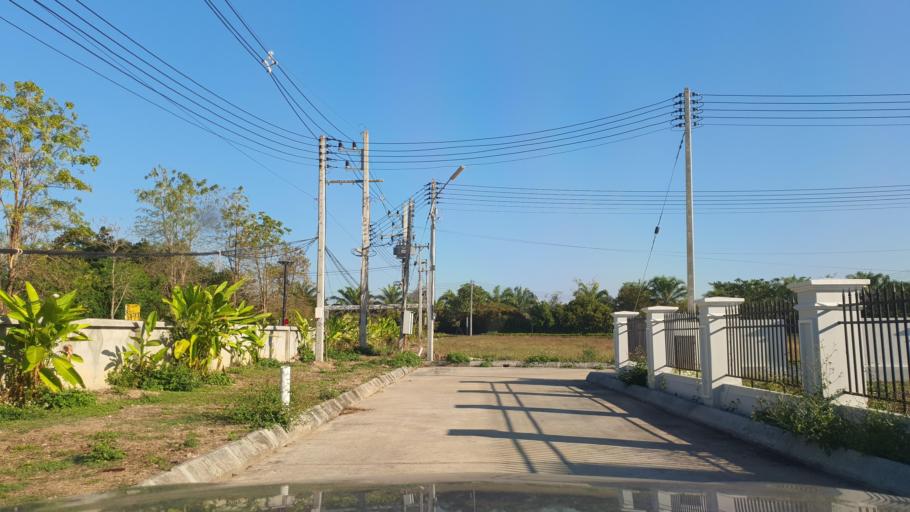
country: TH
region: Chiang Mai
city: Hang Dong
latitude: 18.6973
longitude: 98.9595
